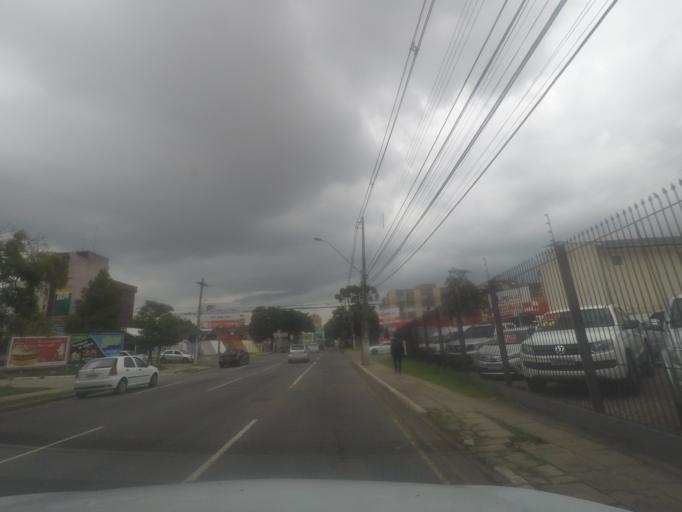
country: BR
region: Parana
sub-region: Curitiba
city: Curitiba
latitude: -25.4826
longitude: -49.2957
